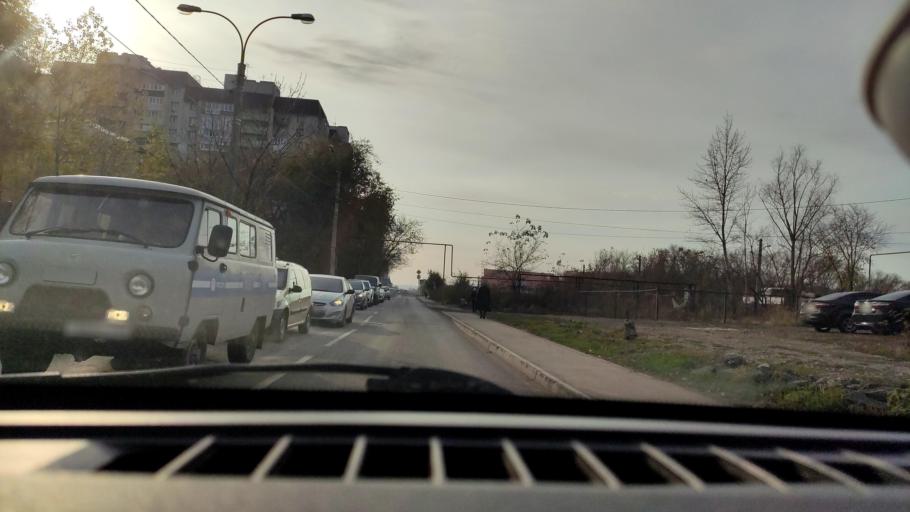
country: RU
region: Samara
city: Samara
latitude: 53.2116
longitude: 50.2028
